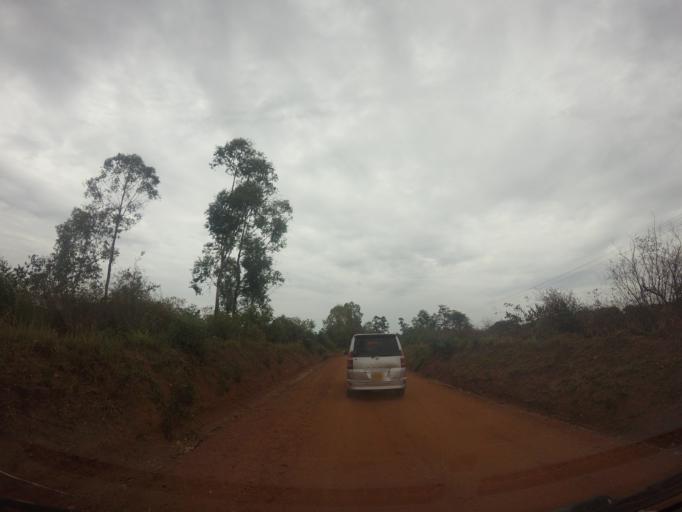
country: UG
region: Northern Region
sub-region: Arua District
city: Arua
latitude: 2.7949
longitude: 30.8724
